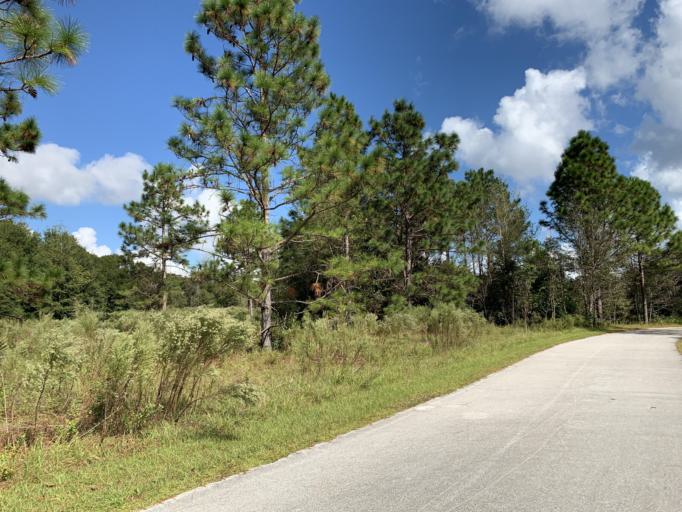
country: US
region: Florida
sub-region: Marion County
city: Silver Springs Shores
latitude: 29.1546
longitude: -82.0443
